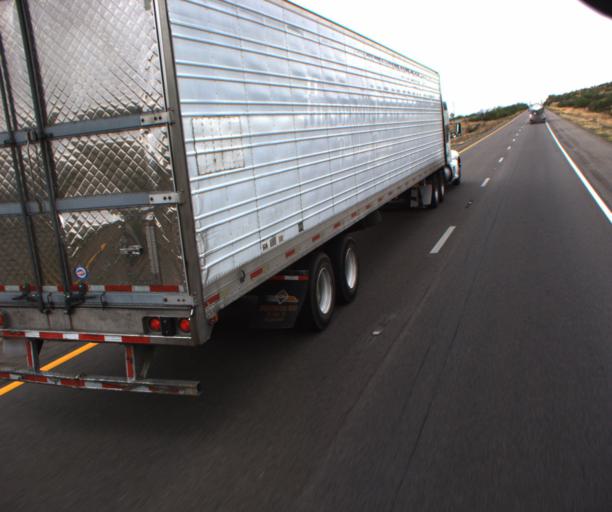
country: US
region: Arizona
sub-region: Cochise County
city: Saint David
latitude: 32.0114
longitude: -110.1258
